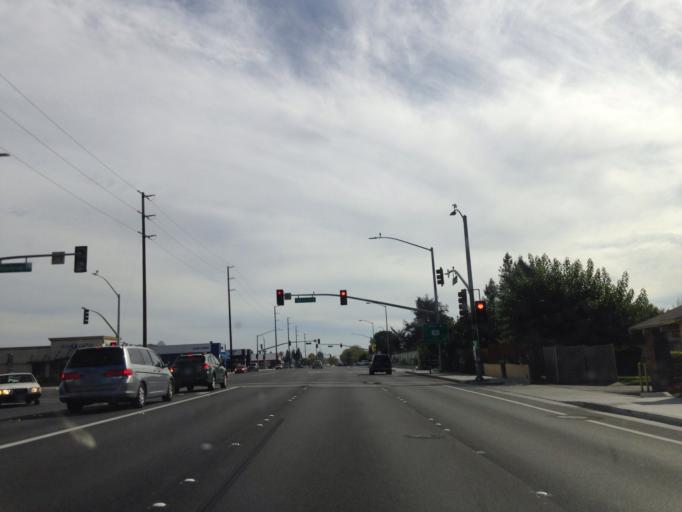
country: US
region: California
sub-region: Sonoma County
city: Roseland
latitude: 38.4169
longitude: -122.7136
